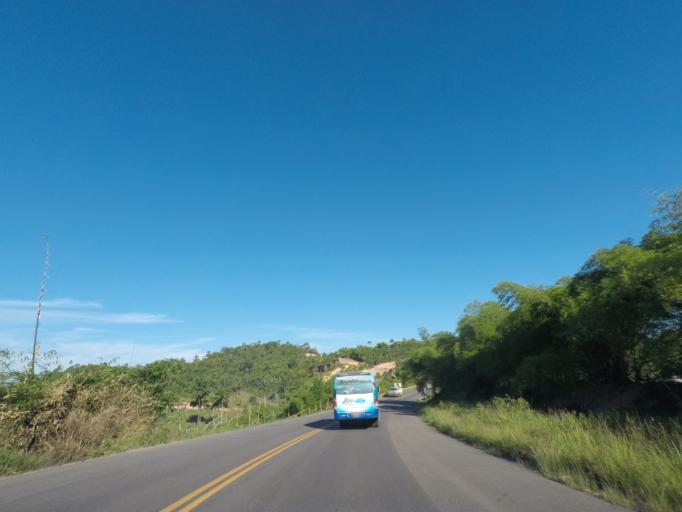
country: BR
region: Bahia
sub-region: Nazare
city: Nazare
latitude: -13.0250
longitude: -38.9983
